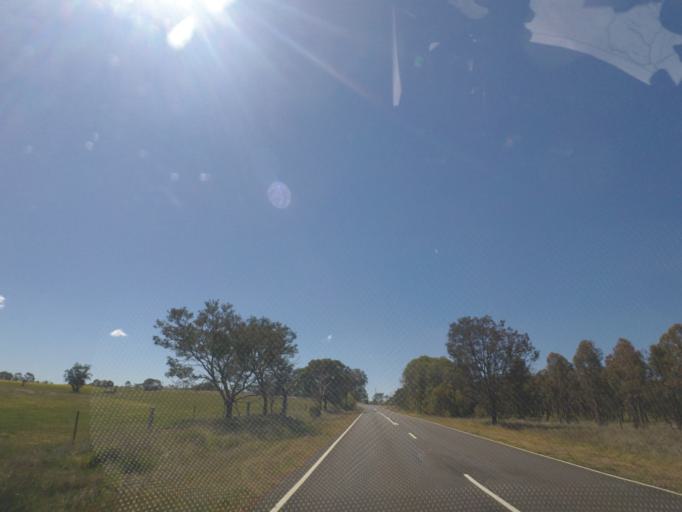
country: AU
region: Victoria
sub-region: Hume
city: Sunbury
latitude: -37.1245
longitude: 144.7686
